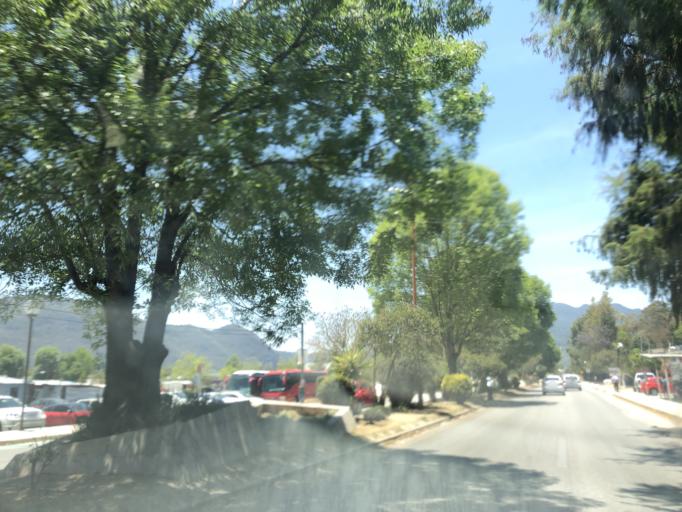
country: MX
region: Chiapas
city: San Cristobal de las Casas
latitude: 16.7309
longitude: -92.6423
